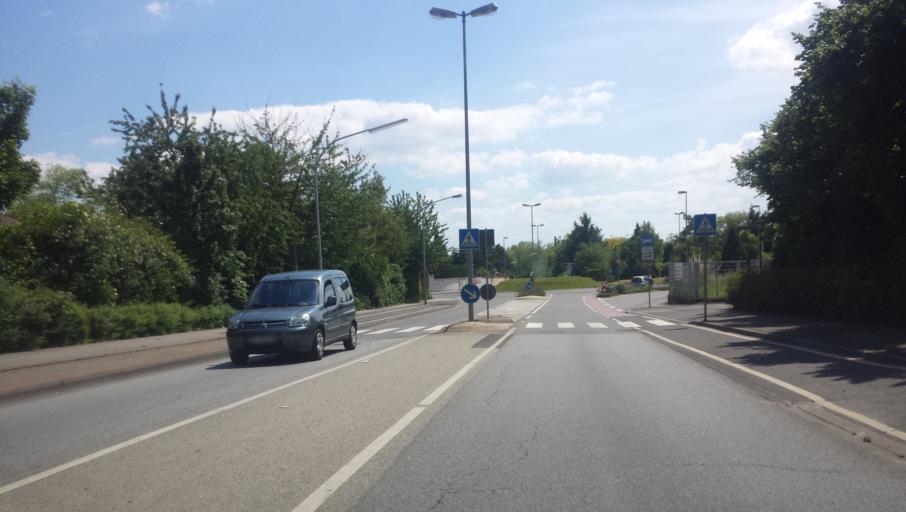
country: DE
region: Rheinland-Pfalz
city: Worms
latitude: 49.6269
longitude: 8.3480
